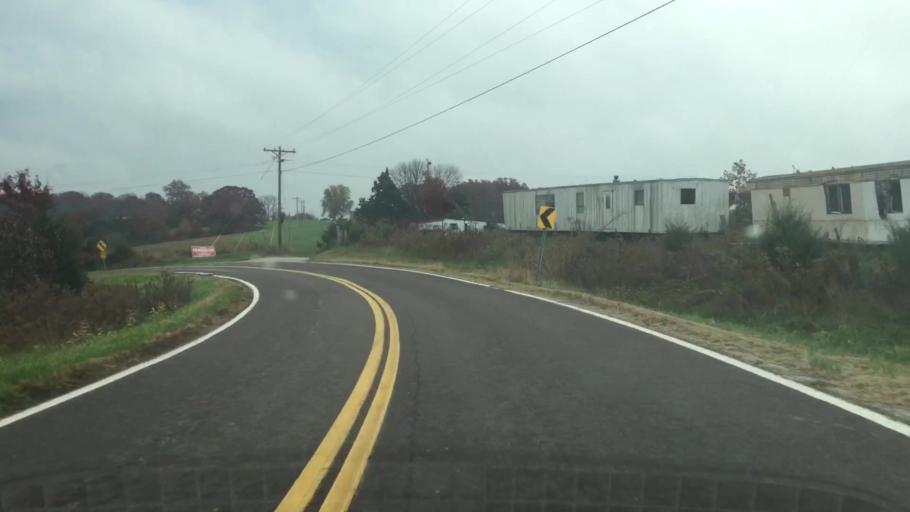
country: US
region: Missouri
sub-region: Callaway County
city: Fulton
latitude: 38.7934
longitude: -91.8837
